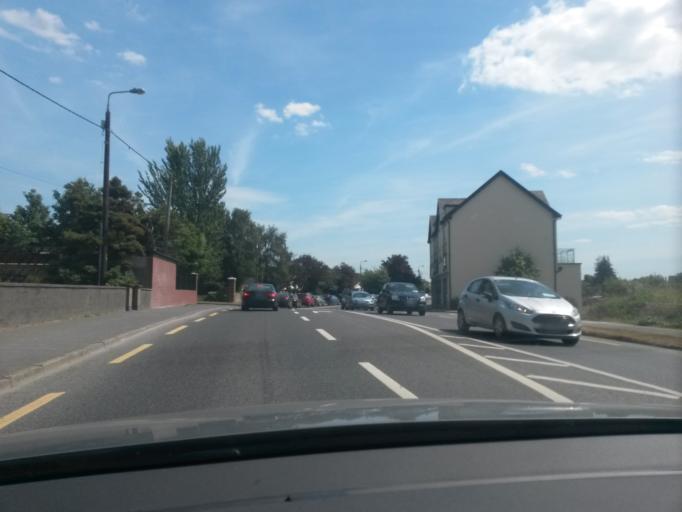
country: IE
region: Leinster
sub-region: Kildare
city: Sallins
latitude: 53.2527
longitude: -6.6659
